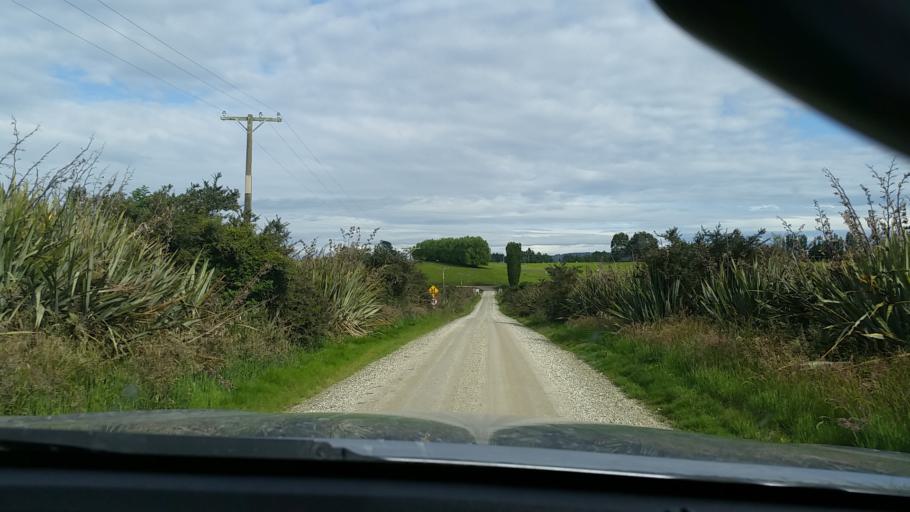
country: NZ
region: Southland
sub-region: Gore District
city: Gore
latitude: -46.2065
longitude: 168.7696
